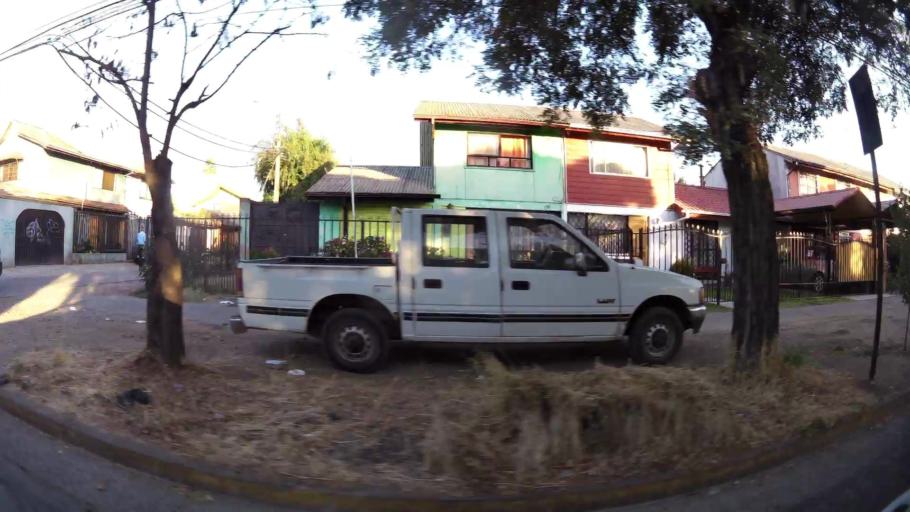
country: CL
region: Maule
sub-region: Provincia de Talca
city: Talca
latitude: -35.4419
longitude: -71.6785
